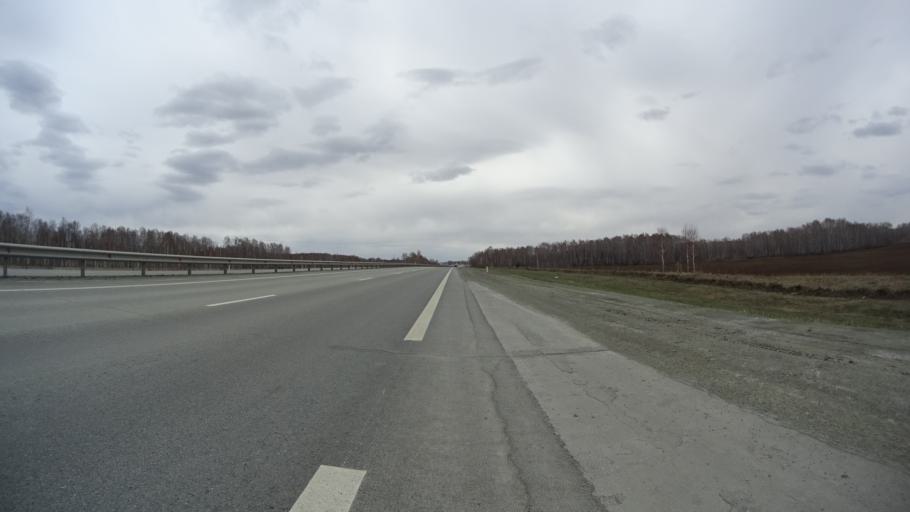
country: RU
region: Chelyabinsk
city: Yemanzhelinka
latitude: 54.8313
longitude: 61.3117
